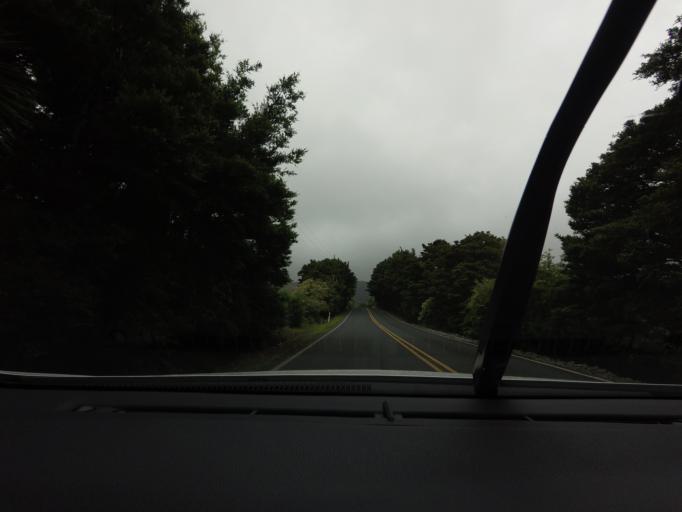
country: NZ
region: Auckland
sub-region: Auckland
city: Wellsford
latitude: -36.2877
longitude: 174.6299
